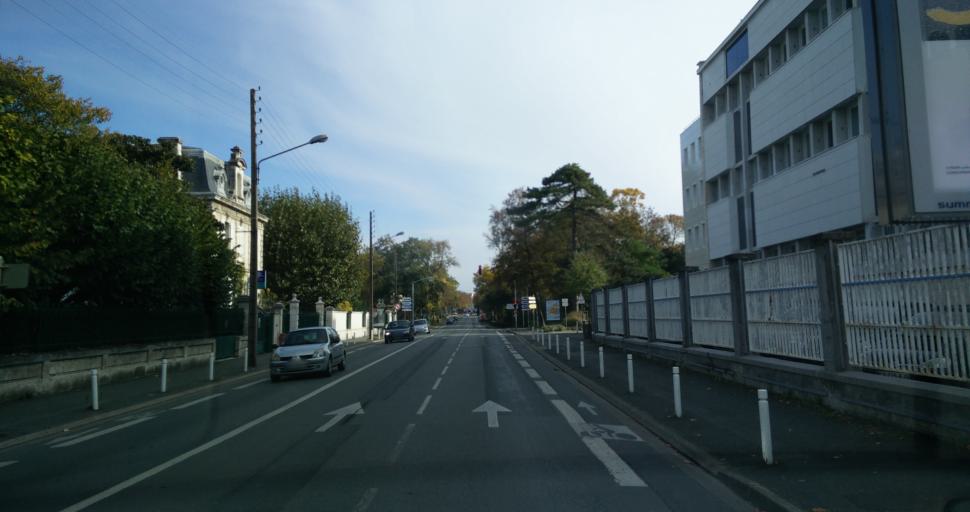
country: FR
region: Poitou-Charentes
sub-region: Departement de la Charente-Maritime
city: La Rochelle
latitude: 46.1626
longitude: -1.1598
